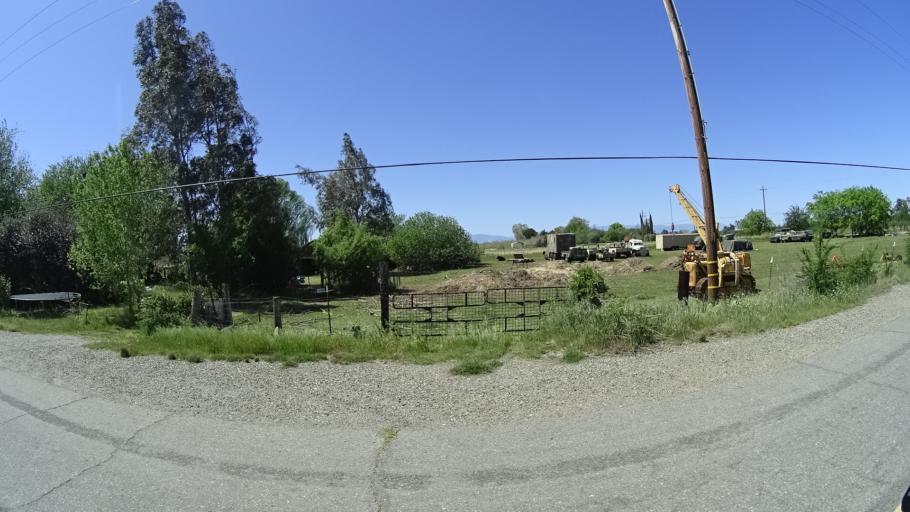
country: US
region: California
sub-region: Glenn County
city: Orland
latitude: 39.7885
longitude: -122.2065
